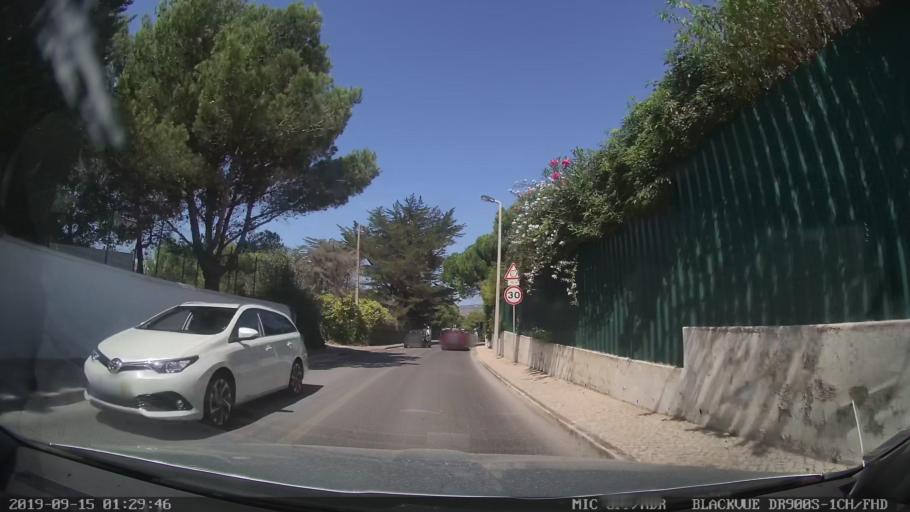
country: PT
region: Lisbon
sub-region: Cascais
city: Cascais
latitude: 38.7205
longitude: -9.4655
